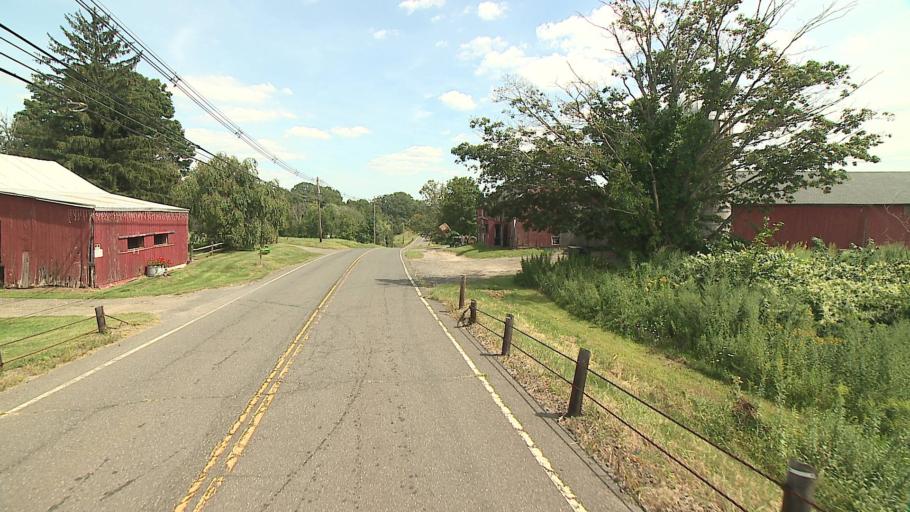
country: US
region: Connecticut
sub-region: Litchfield County
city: Bethlehem Village
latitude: 41.6202
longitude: -73.2413
